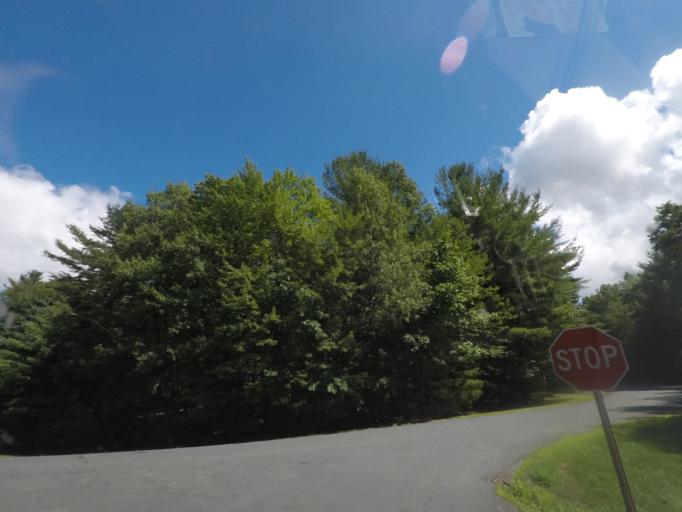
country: US
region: New York
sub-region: Rensselaer County
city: Averill Park
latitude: 42.6262
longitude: -73.5829
